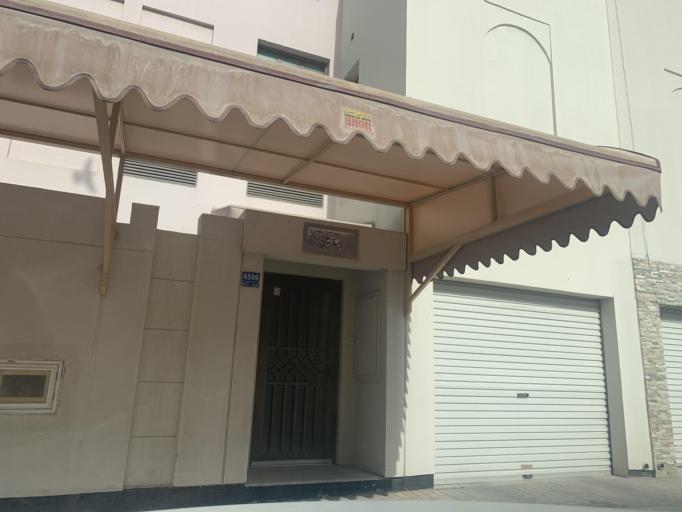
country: BH
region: Northern
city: Sitrah
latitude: 26.1580
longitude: 50.6273
